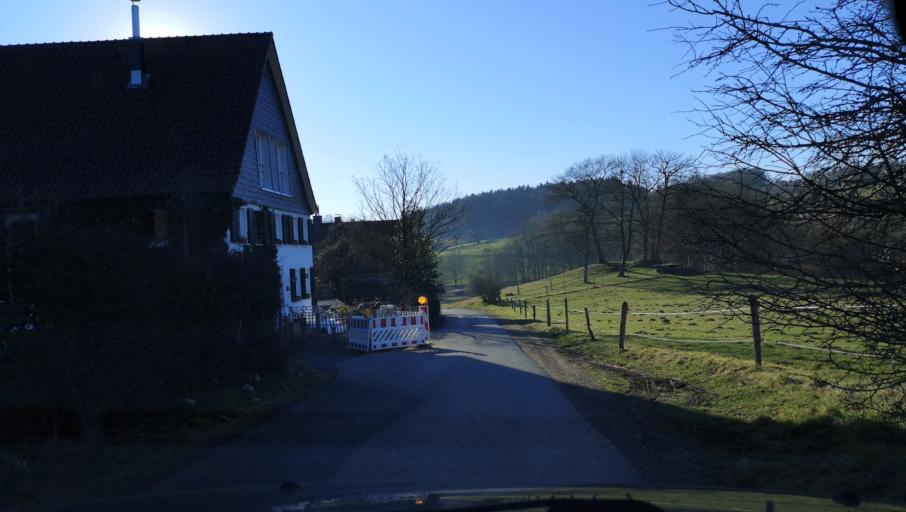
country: DE
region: North Rhine-Westphalia
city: Radevormwald
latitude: 51.2154
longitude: 7.4089
